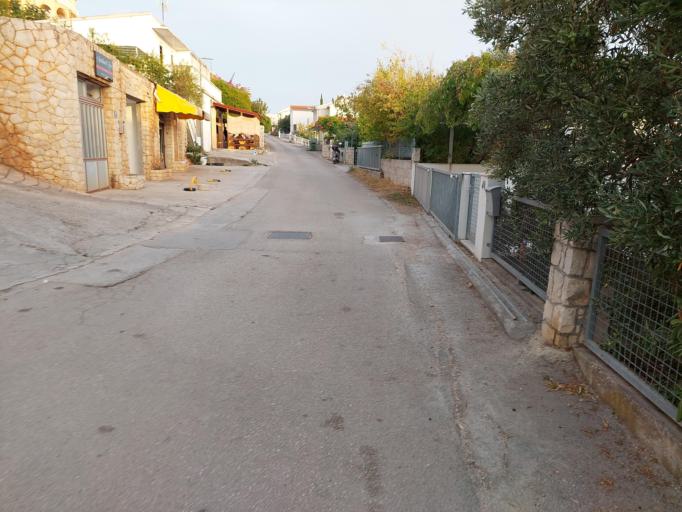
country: HR
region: Splitsko-Dalmatinska
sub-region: Grad Trogir
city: Trogir
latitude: 43.4916
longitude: 16.2777
